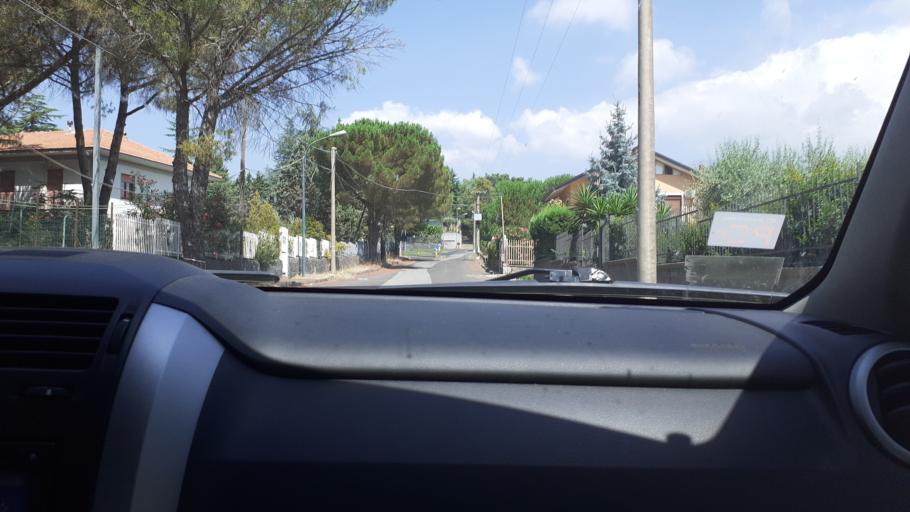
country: IT
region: Sicily
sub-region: Catania
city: Nicolosi
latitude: 37.6237
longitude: 15.0256
